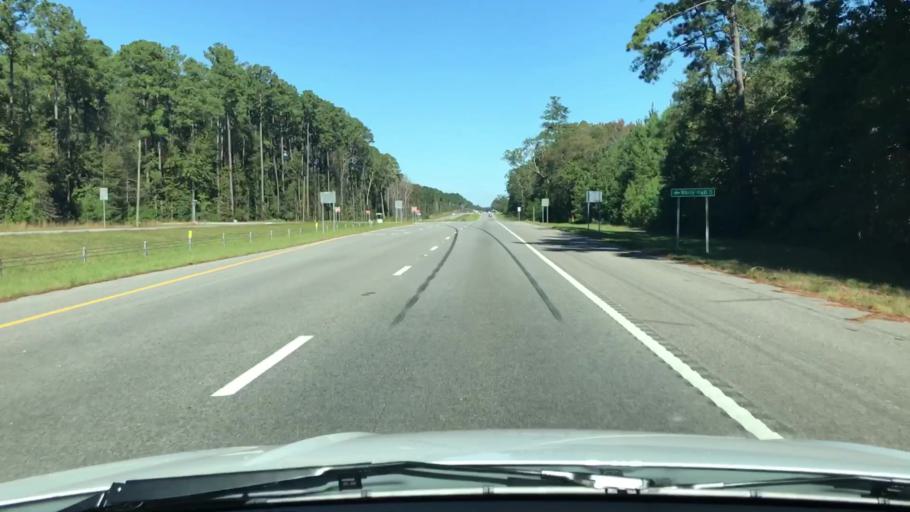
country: US
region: South Carolina
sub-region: Hampton County
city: Yemassee
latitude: 32.6815
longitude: -80.6372
